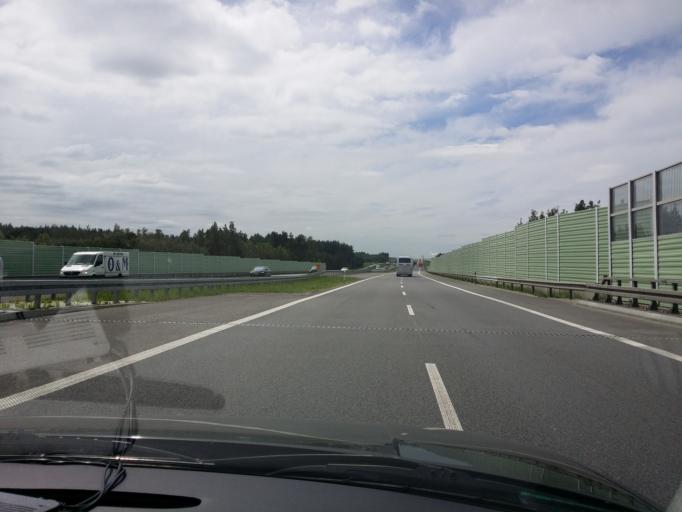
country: PL
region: Masovian Voivodeship
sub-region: Powiat szydlowiecki
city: Oronsko
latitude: 51.3100
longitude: 21.0088
